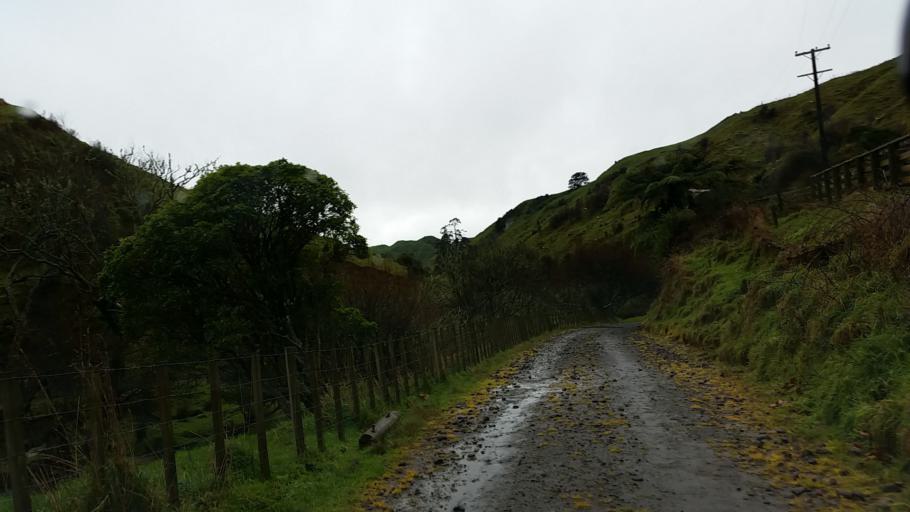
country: NZ
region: Taranaki
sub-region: South Taranaki District
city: Eltham
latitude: -39.4917
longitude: 174.4330
